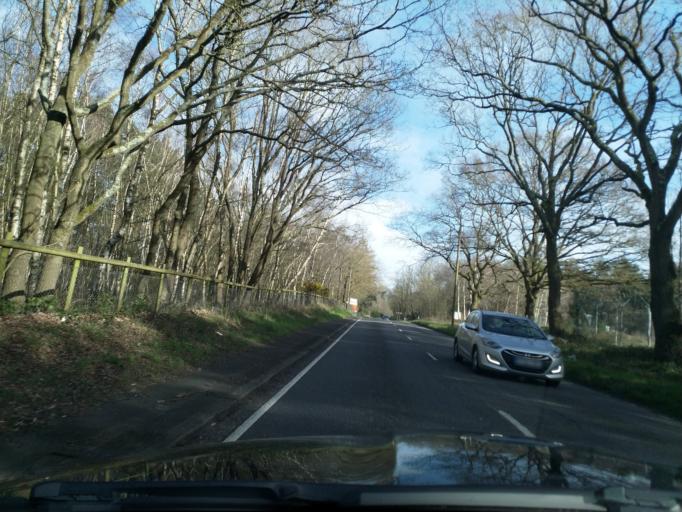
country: GB
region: England
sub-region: Hampshire
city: Aldershot
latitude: 51.2668
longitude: -0.7874
